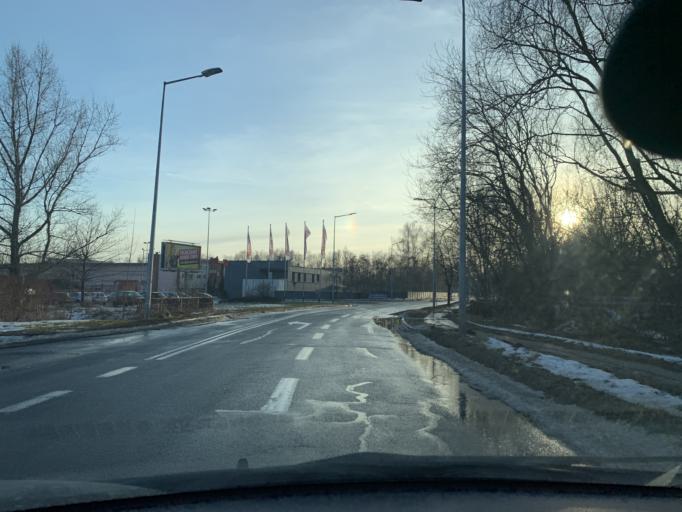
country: PL
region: Silesian Voivodeship
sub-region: Powiat tarnogorski
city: Radzionkow
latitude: 50.3818
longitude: 18.8892
